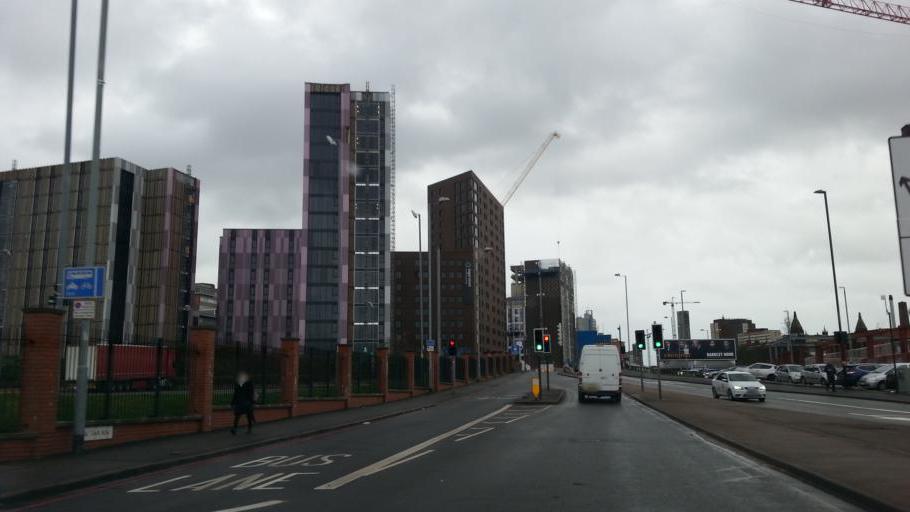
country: GB
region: England
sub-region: City and Borough of Birmingham
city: Birmingham
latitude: 52.4899
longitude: -1.8948
